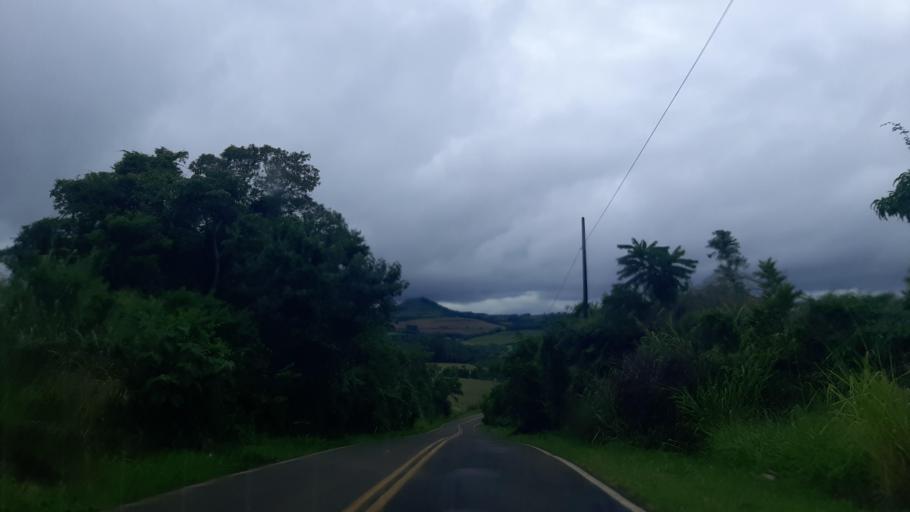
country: BR
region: Parana
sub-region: Ampere
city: Ampere
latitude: -25.9904
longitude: -53.4387
